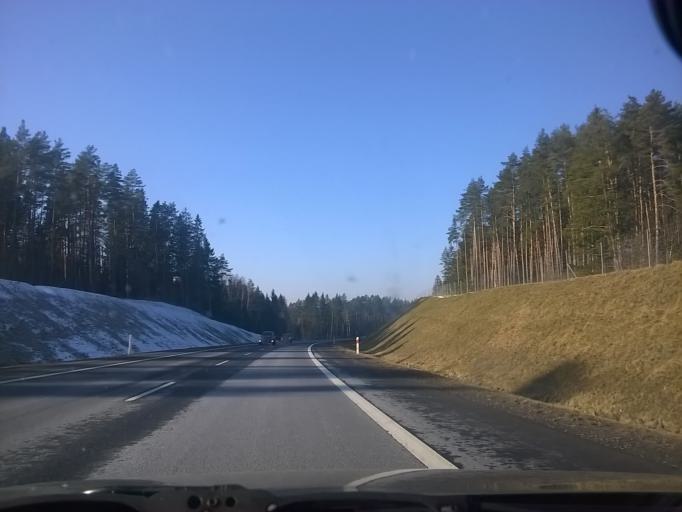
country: PL
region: Warmian-Masurian Voivodeship
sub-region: Powiat olsztynski
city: Barczewo
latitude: 53.8292
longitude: 20.7809
